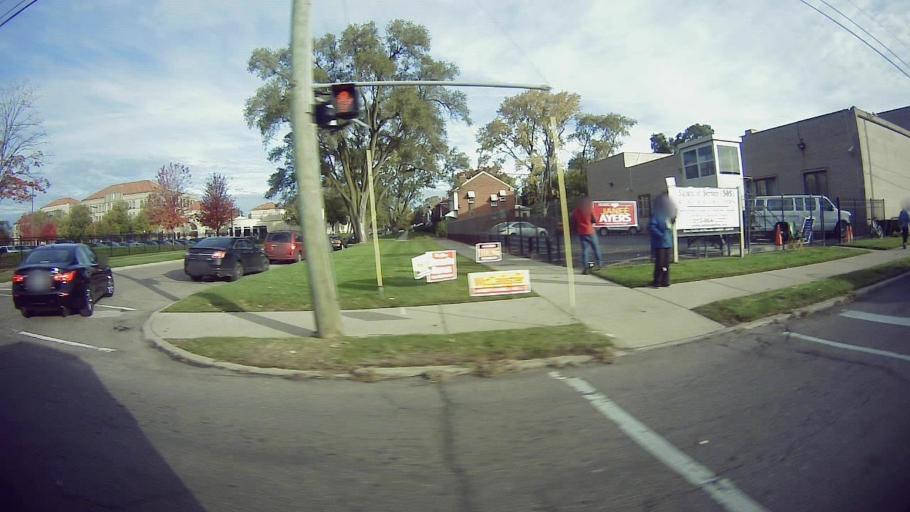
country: US
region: Michigan
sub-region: Oakland County
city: Ferndale
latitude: 42.4314
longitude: -83.1529
